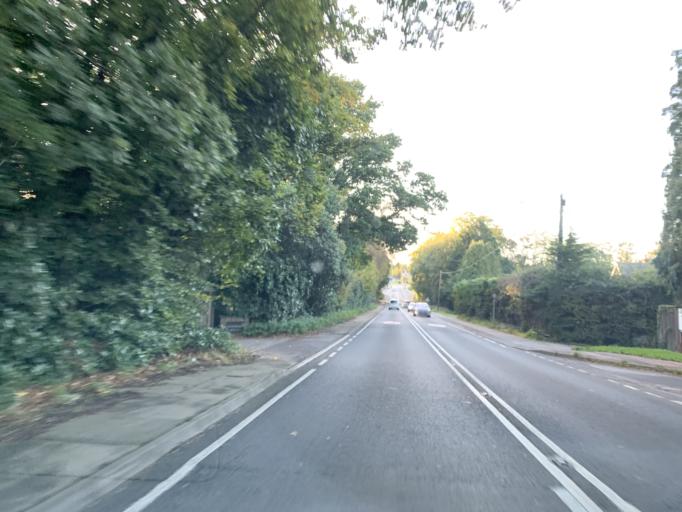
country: GB
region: England
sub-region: Hampshire
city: West Wellow
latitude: 50.9677
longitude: -1.5815
